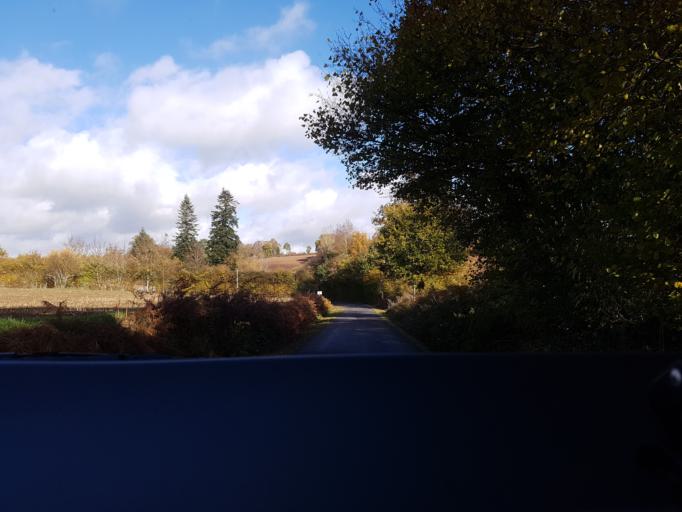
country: FR
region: Lower Normandy
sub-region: Departement de l'Orne
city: Champsecret
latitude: 48.6348
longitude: -0.5806
